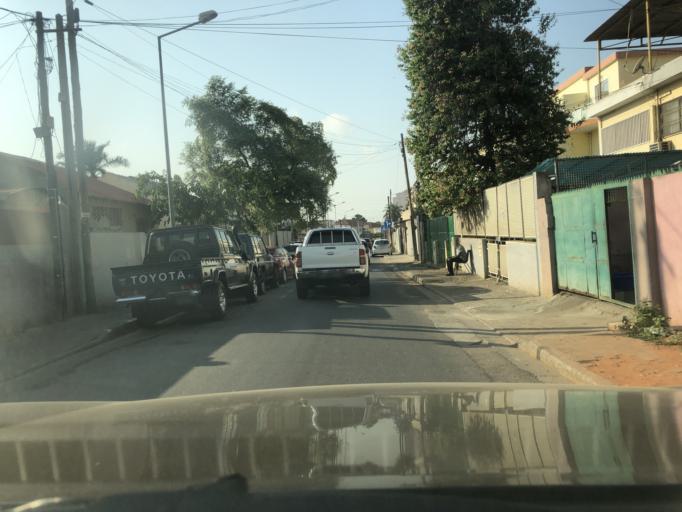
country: AO
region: Luanda
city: Luanda
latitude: -8.8261
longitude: 13.2514
